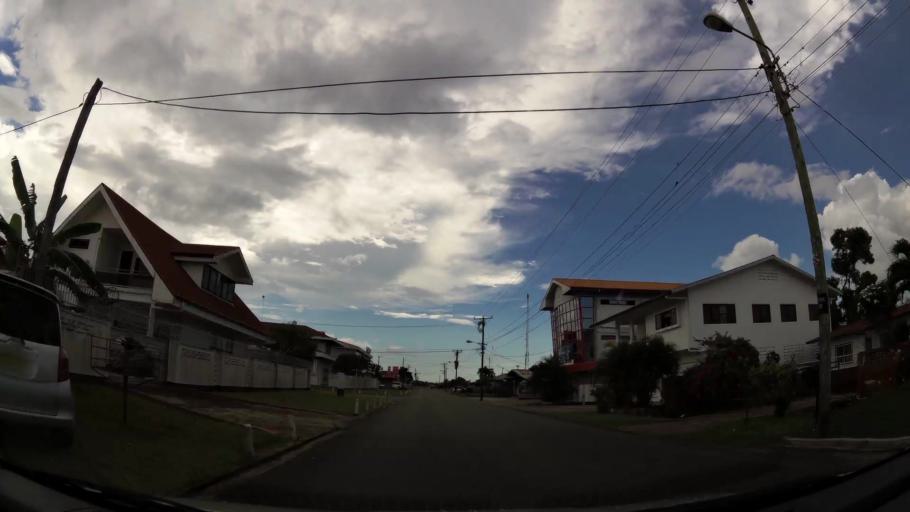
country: SR
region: Paramaribo
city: Paramaribo
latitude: 5.8482
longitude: -55.1334
